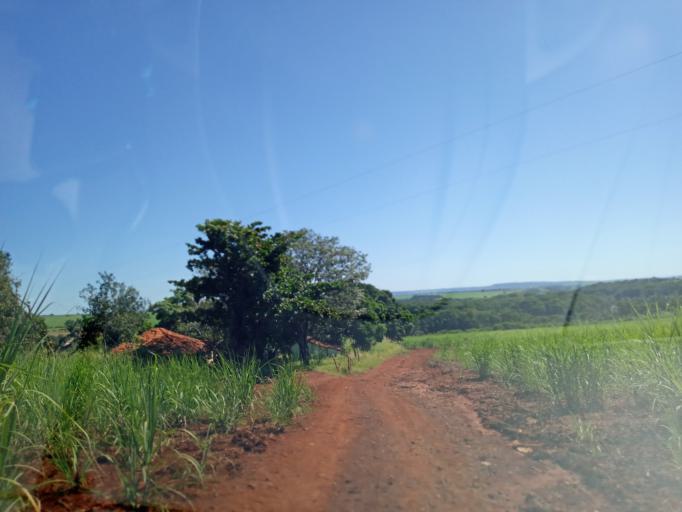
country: BR
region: Goias
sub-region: Itumbiara
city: Itumbiara
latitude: -18.4231
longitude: -49.1669
